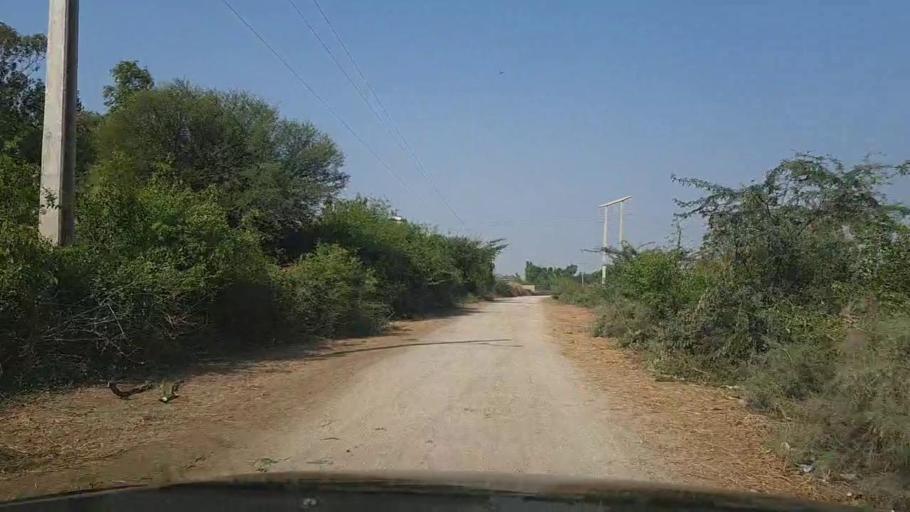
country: PK
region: Sindh
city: Thatta
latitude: 24.6126
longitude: 67.8218
